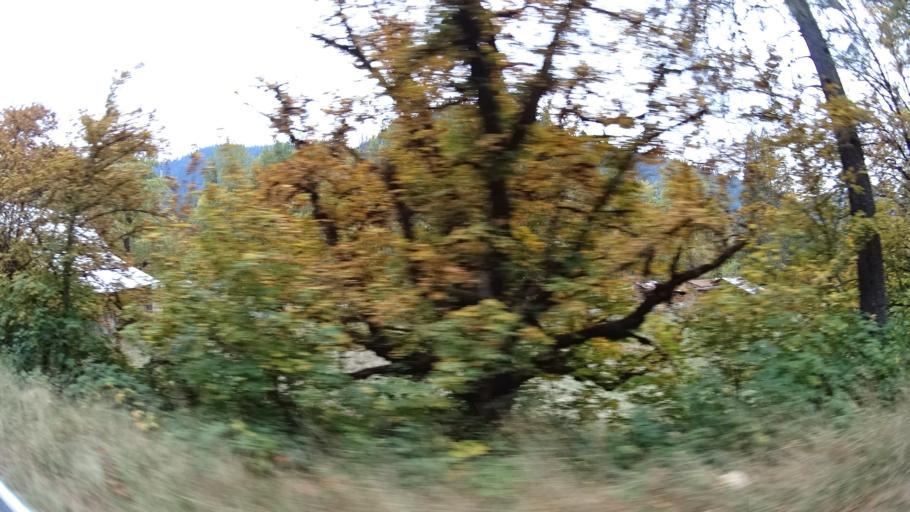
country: US
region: California
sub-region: Siskiyou County
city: Happy Camp
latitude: 41.8711
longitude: -123.4059
